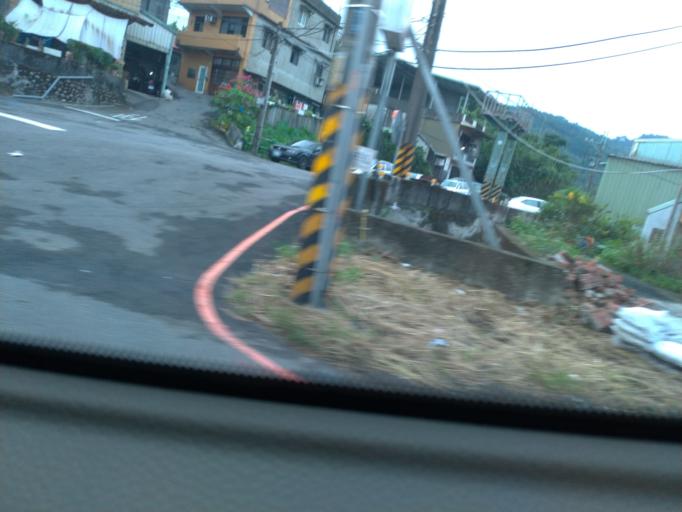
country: TW
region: Taiwan
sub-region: Taoyuan
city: Taoyuan
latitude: 24.9344
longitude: 121.3894
